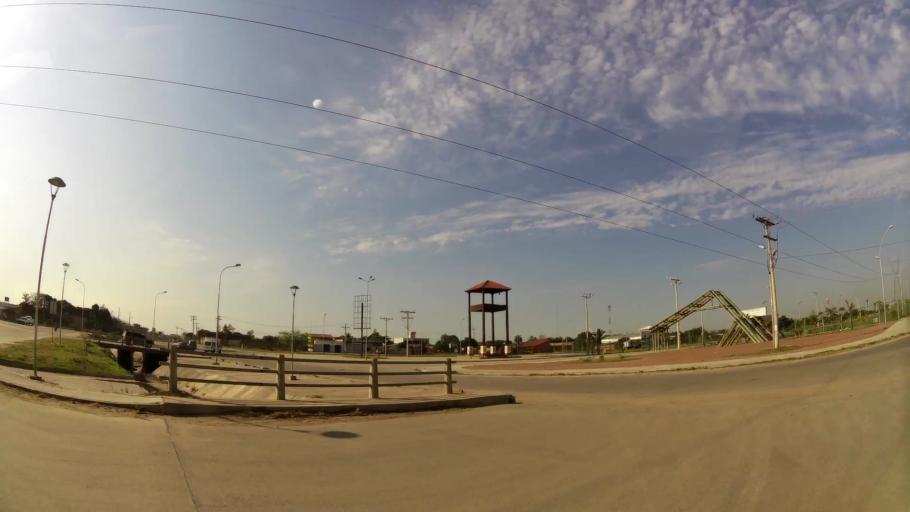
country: BO
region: Santa Cruz
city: Santa Cruz de la Sierra
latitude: -17.7279
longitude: -63.1367
